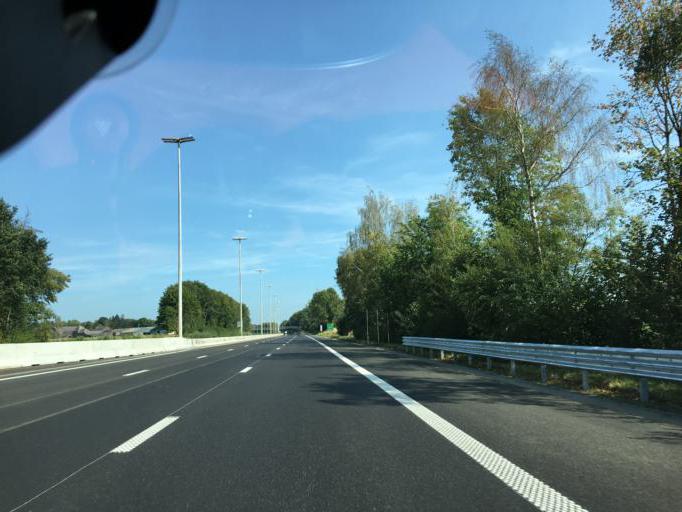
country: BE
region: Wallonia
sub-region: Province de Namur
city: Noville-les-Bois
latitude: 50.5304
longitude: 4.9677
